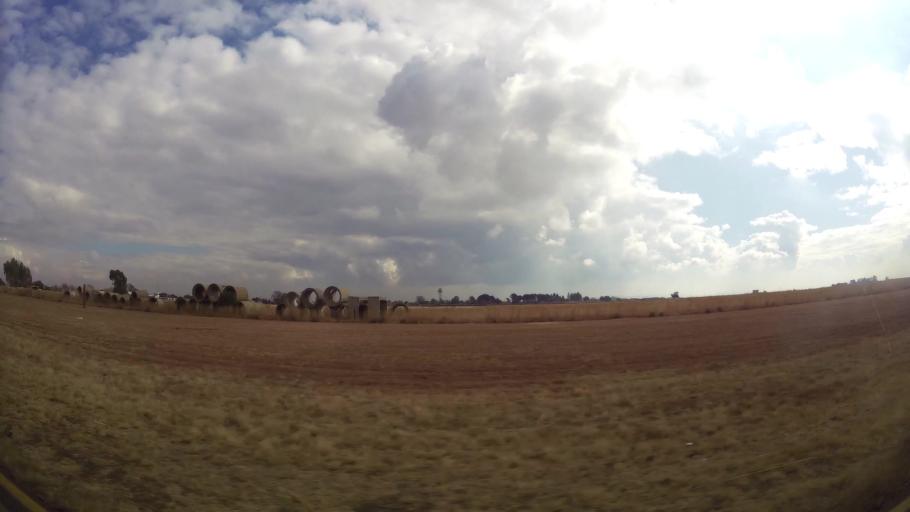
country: ZA
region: Gauteng
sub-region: Sedibeng District Municipality
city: Meyerton
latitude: -26.6143
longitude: 28.0641
